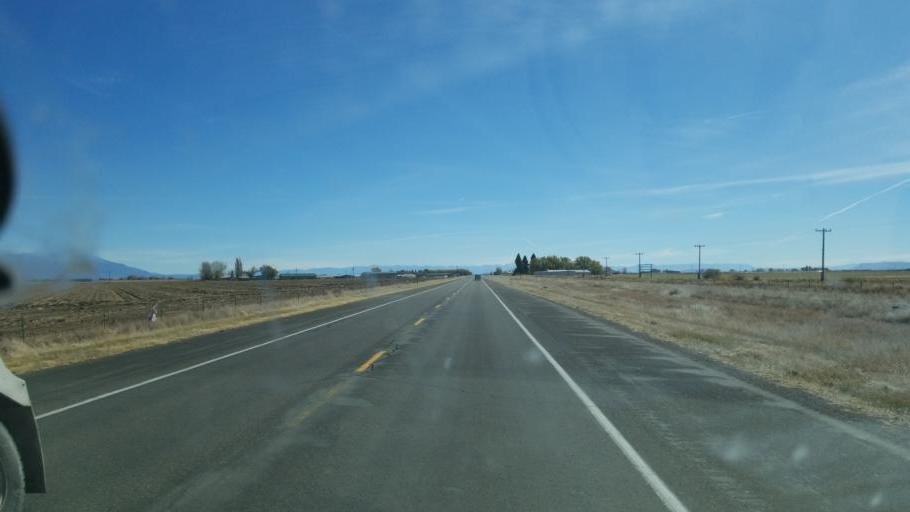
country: US
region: Colorado
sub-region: Rio Grande County
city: Monte Vista
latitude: 37.5547
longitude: -106.0824
